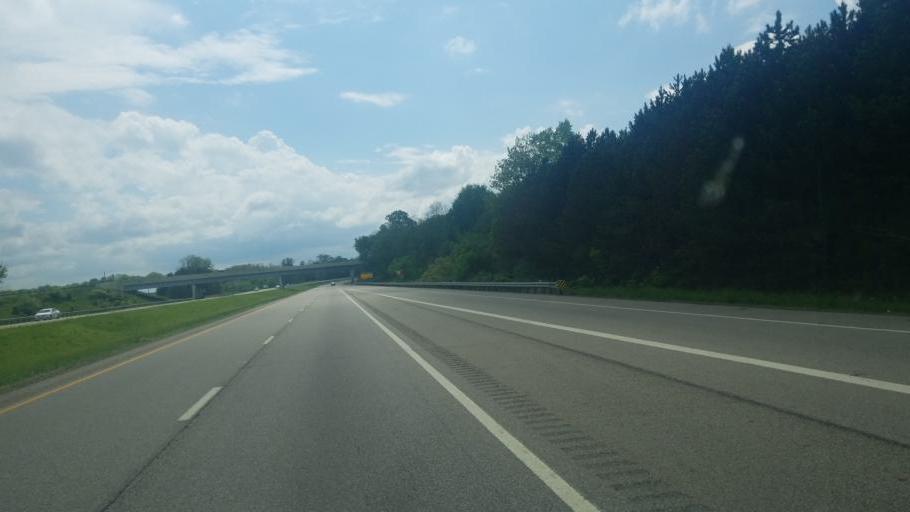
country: US
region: Ohio
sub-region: Trumbull County
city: Hubbard
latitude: 41.1615
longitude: -80.6154
